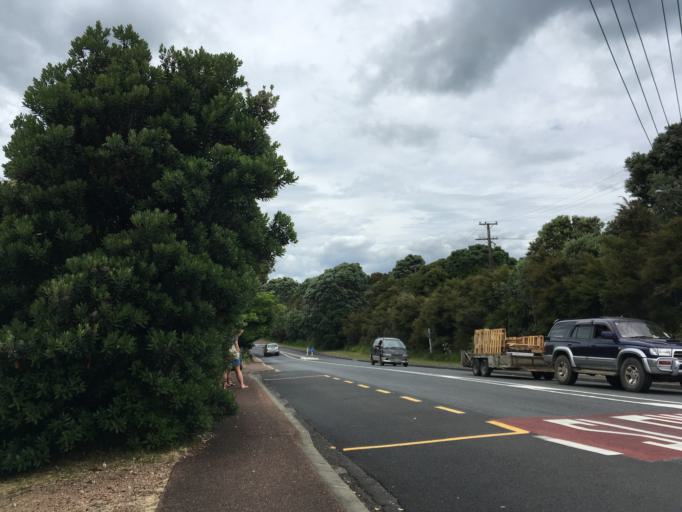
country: NZ
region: Auckland
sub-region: Auckland
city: Pakuranga
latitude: -36.7968
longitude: 175.0325
